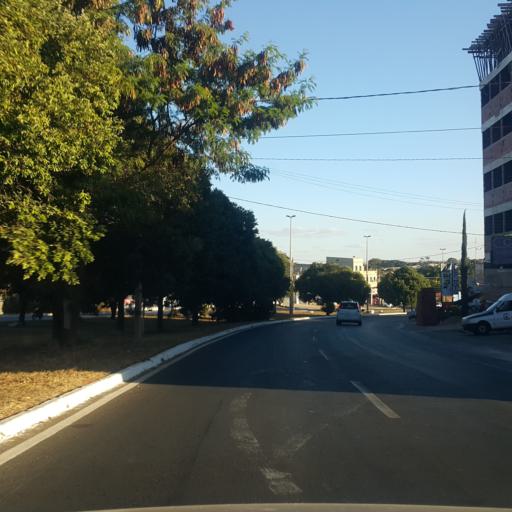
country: BR
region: Federal District
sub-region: Brasilia
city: Brasilia
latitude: -15.8542
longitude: -47.9752
